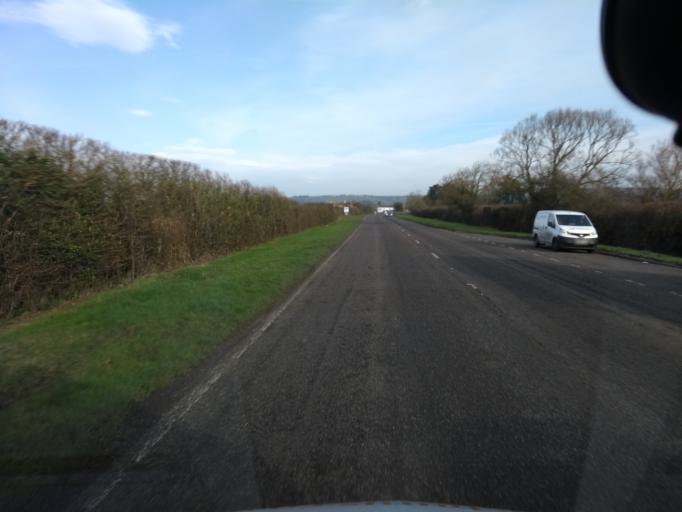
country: GB
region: England
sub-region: North Somerset
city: Bleadon
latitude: 51.2727
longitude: -2.9336
